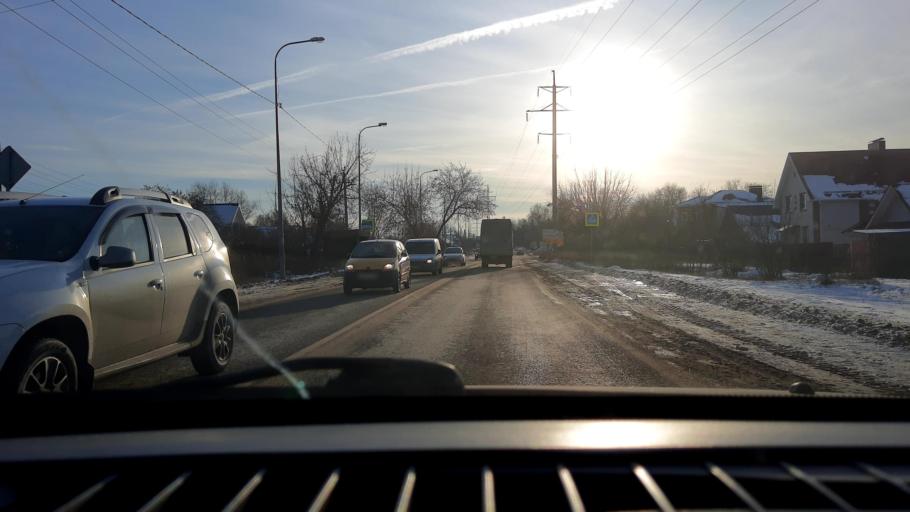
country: RU
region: Nizjnij Novgorod
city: Bor
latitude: 56.3662
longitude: 44.0708
